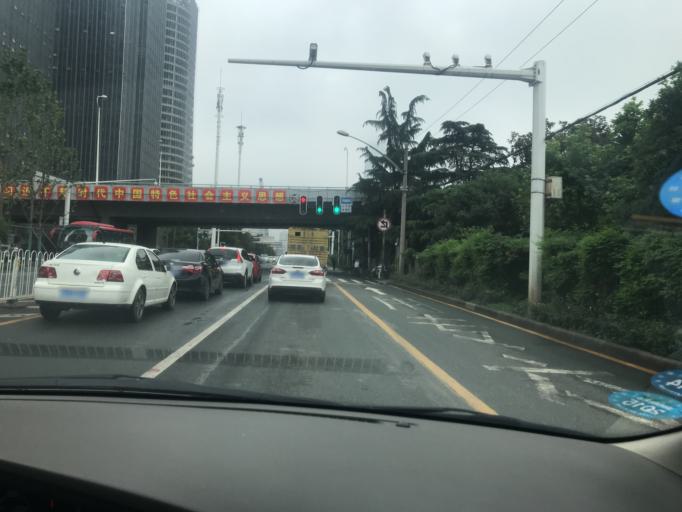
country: CN
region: Hubei
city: Jiang'an
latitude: 30.5974
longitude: 114.3327
